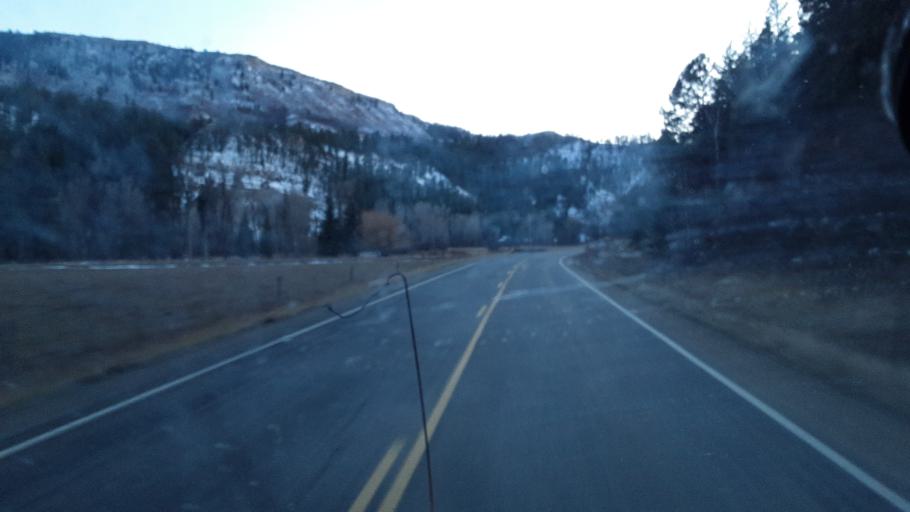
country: US
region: Colorado
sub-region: La Plata County
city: Durango
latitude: 37.3303
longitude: -107.7455
